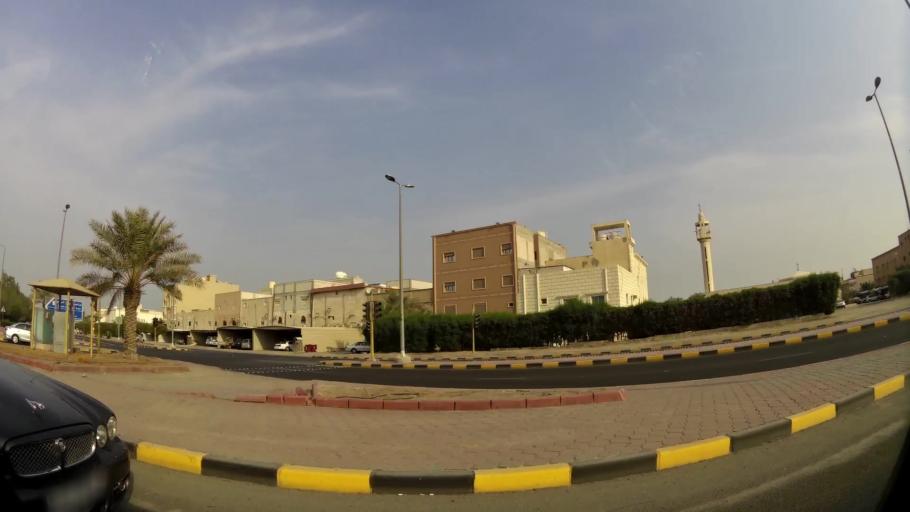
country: KW
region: Mubarak al Kabir
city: Sabah as Salim
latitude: 29.2529
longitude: 48.0558
